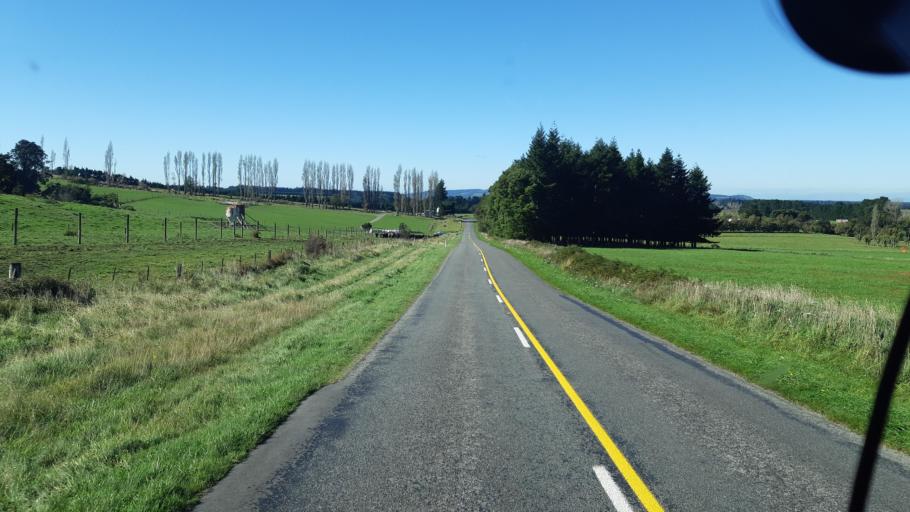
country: NZ
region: Canterbury
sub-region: Waimakariri District
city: Oxford
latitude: -43.2283
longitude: 172.2426
